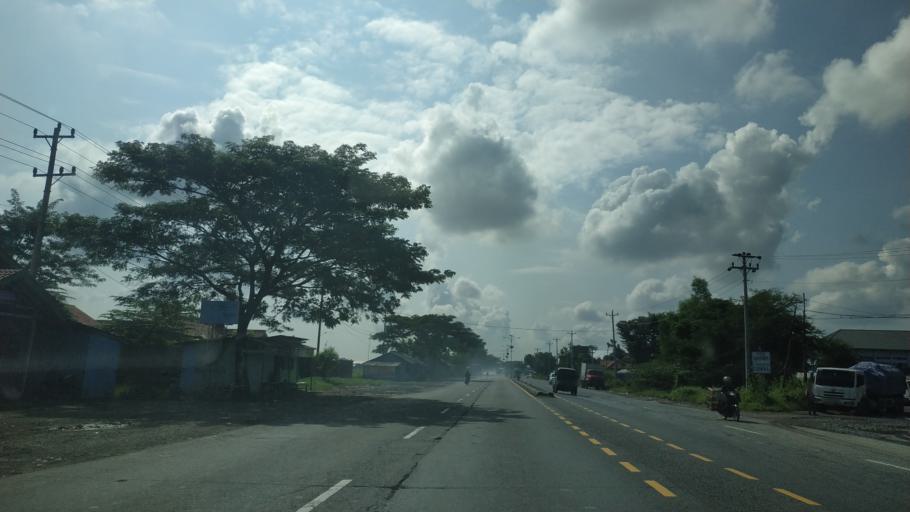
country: ID
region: Central Java
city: Comal
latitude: -6.9006
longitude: 109.5042
